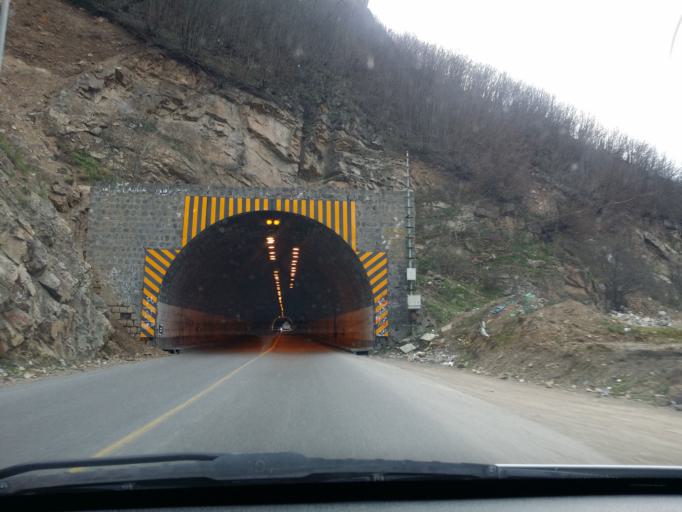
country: IR
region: Mazandaran
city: Chalus
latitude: 36.2627
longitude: 51.2708
